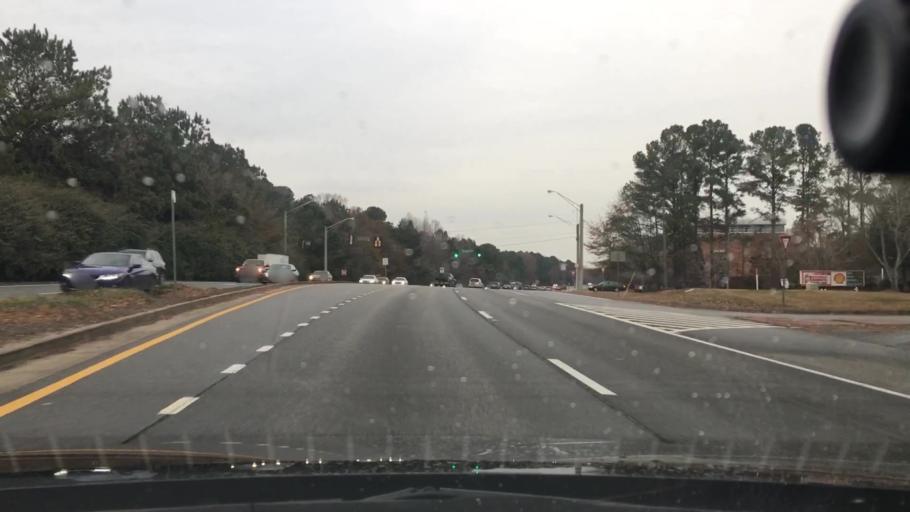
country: US
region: Georgia
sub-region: Fayette County
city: Peachtree City
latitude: 33.4079
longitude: -84.6013
